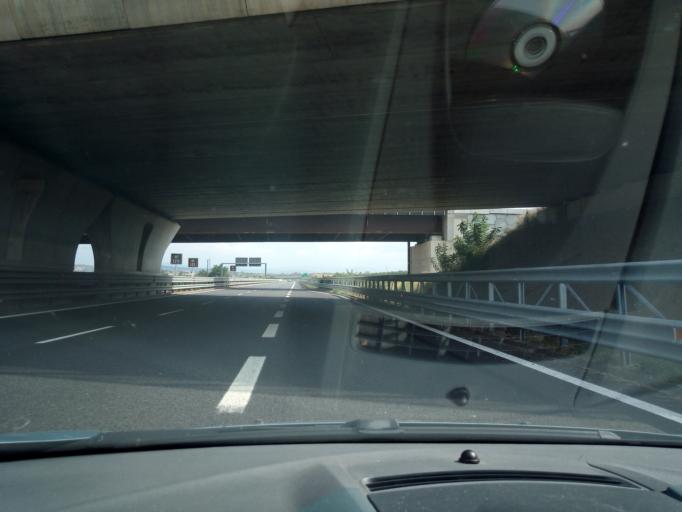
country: IT
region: Calabria
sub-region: Provincia di Cosenza
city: Firmo
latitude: 39.7215
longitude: 16.2389
